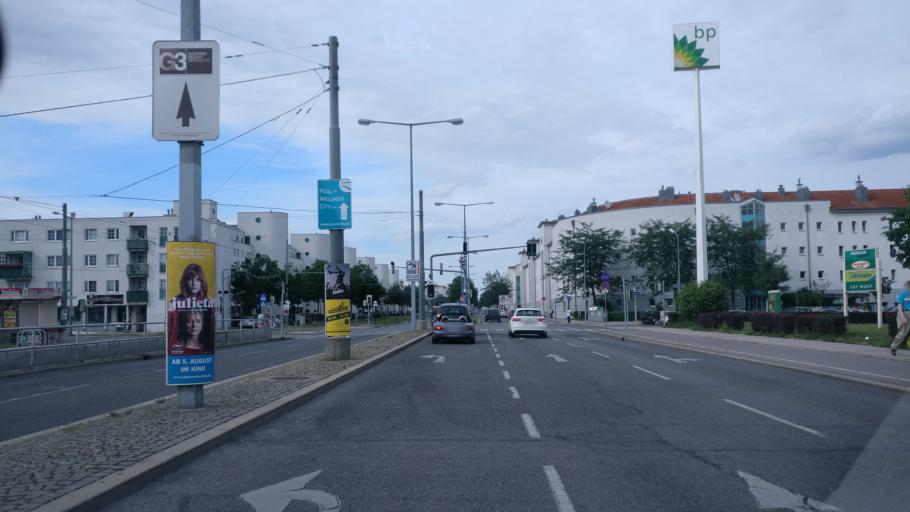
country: AT
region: Lower Austria
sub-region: Politischer Bezirk Korneuburg
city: Hagenbrunn
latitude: 48.2835
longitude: 16.4128
